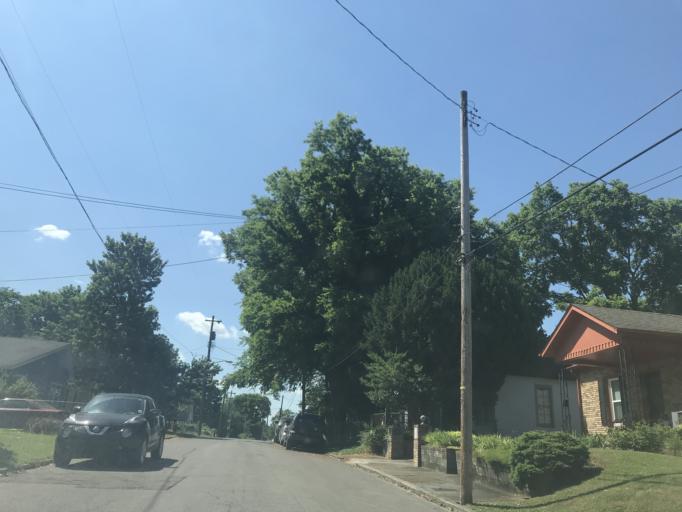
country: US
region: Tennessee
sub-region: Davidson County
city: Nashville
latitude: 36.1816
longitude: -86.8094
